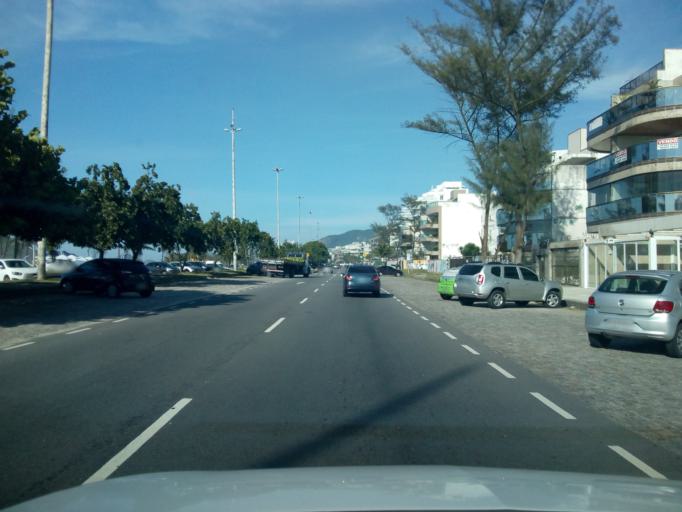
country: BR
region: Rio de Janeiro
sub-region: Nilopolis
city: Nilopolis
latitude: -23.0265
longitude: -43.4624
